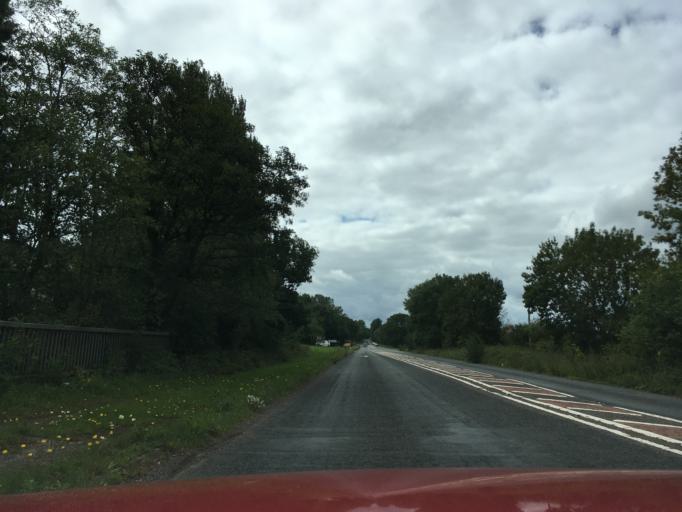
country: GB
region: England
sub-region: Devon
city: Bradninch
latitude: 50.8115
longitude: -3.4210
